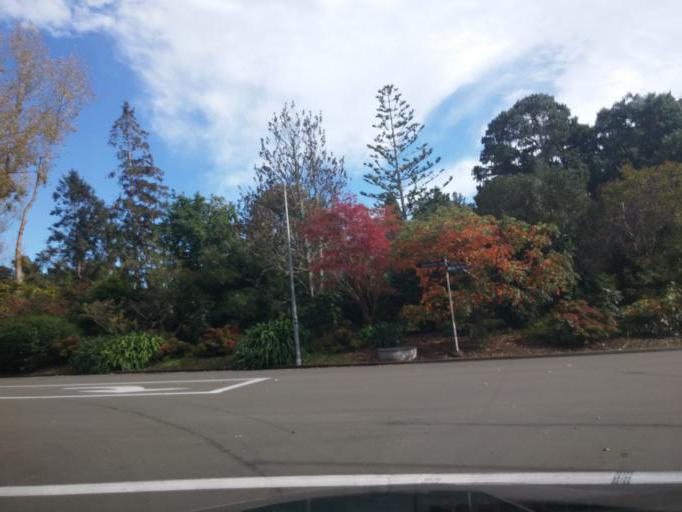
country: NZ
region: Manawatu-Wanganui
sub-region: Palmerston North City
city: Palmerston North
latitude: -40.3845
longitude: 175.6165
